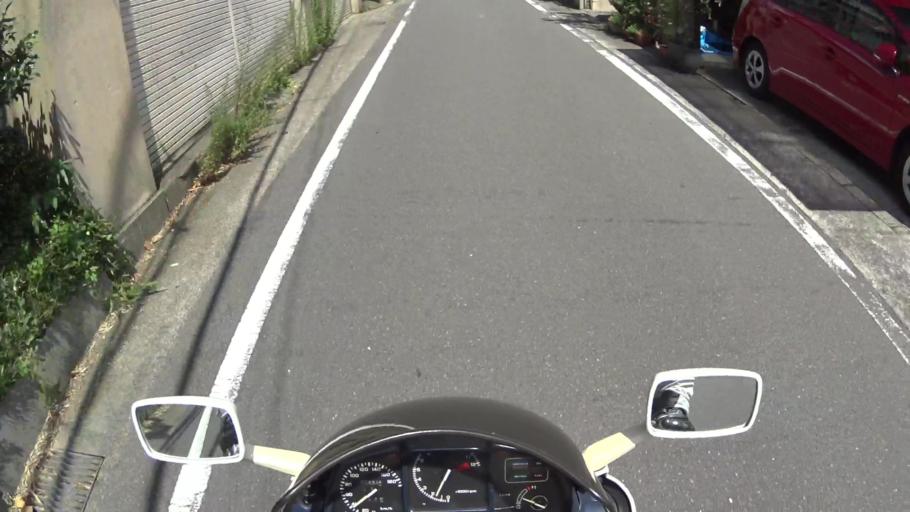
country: JP
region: Kyoto
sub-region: Kyoto-shi
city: Kamigyo-ku
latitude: 35.0760
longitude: 135.7652
